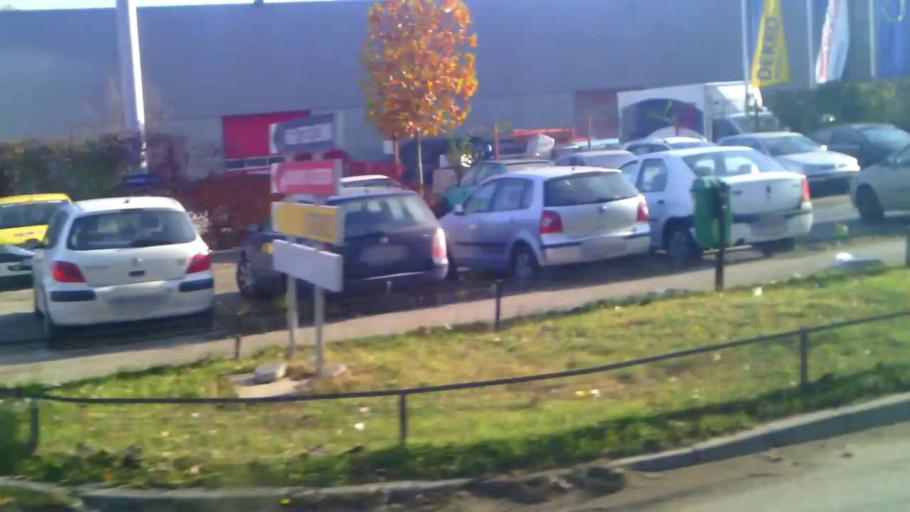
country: RO
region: Ilfov
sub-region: Comuna Popesti-Leordeni
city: Popesti-Leordeni
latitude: 44.3655
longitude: 26.1460
